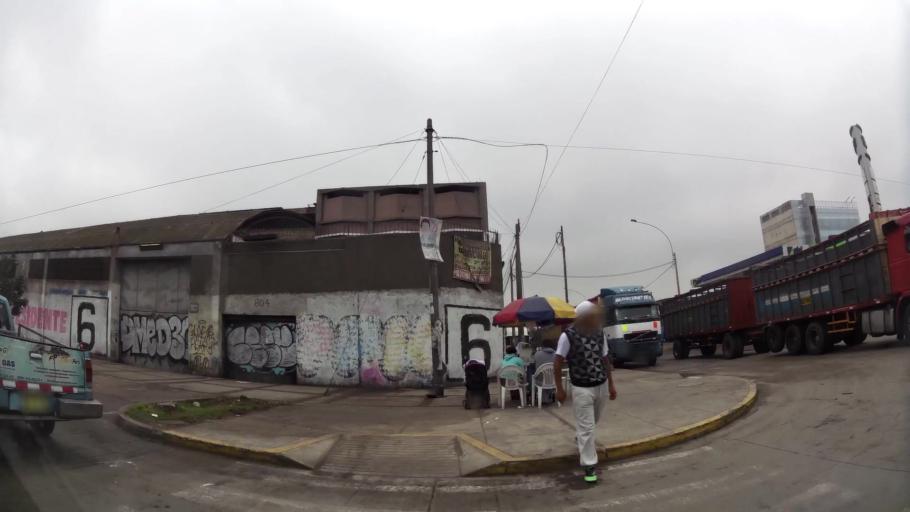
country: PE
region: Lima
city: Lima
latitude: -12.0663
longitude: -77.0223
